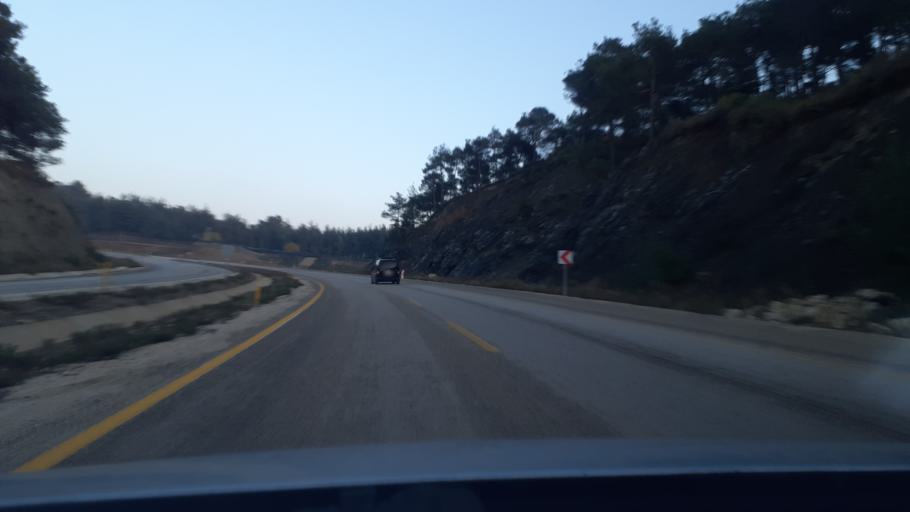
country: TR
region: Hatay
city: Yayladagi
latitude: 35.8906
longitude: 36.0888
